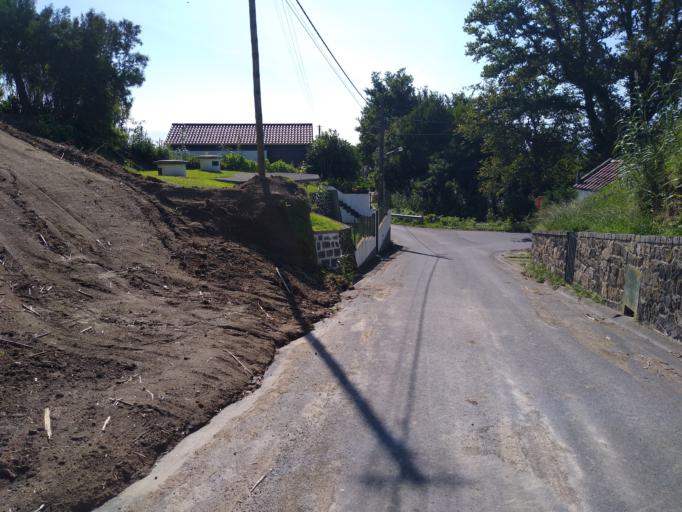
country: PT
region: Azores
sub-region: Ponta Delgada
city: Arrifes
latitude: 37.8392
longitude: -25.8267
